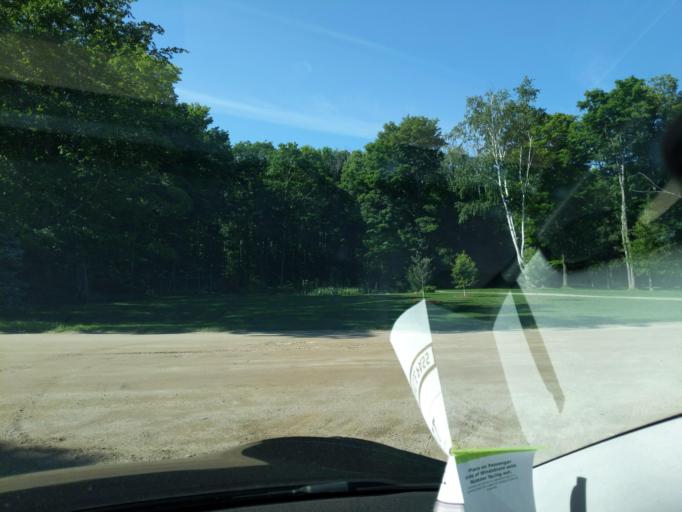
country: US
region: Michigan
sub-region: Mackinac County
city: Saint Ignace
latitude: 45.6988
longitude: -84.7316
